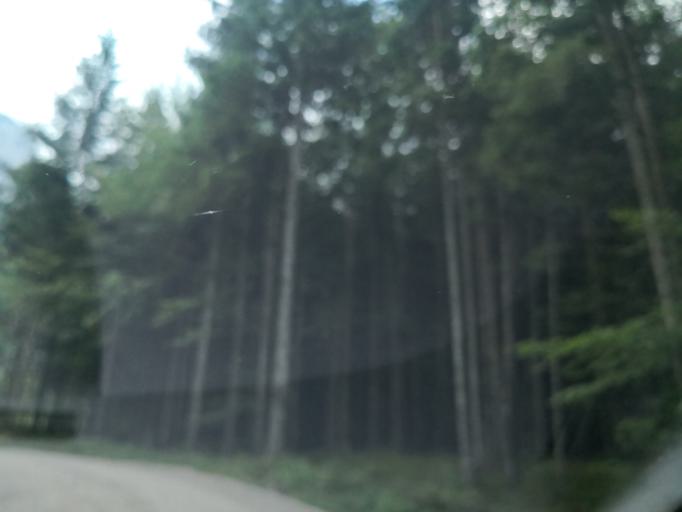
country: SI
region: Jezersko
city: Zgornje Jezersko
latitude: 46.3890
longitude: 14.5348
